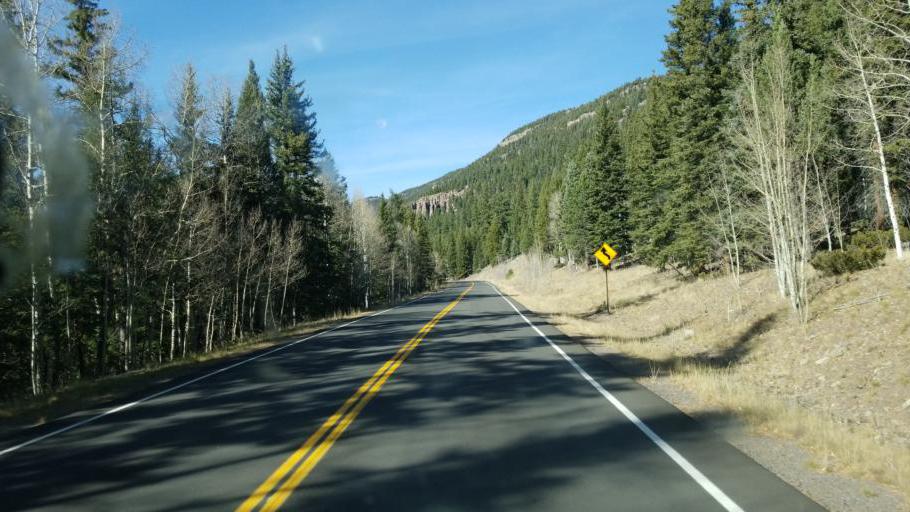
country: US
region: Colorado
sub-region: Conejos County
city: Conejos
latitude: 37.0949
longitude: -106.3051
